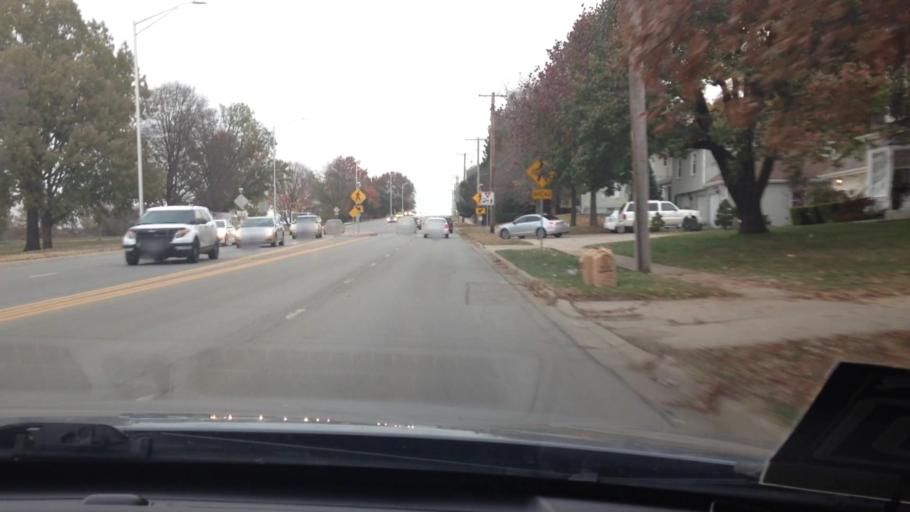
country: US
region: Kansas
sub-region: Johnson County
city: Overland Park
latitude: 38.9620
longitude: -94.6491
